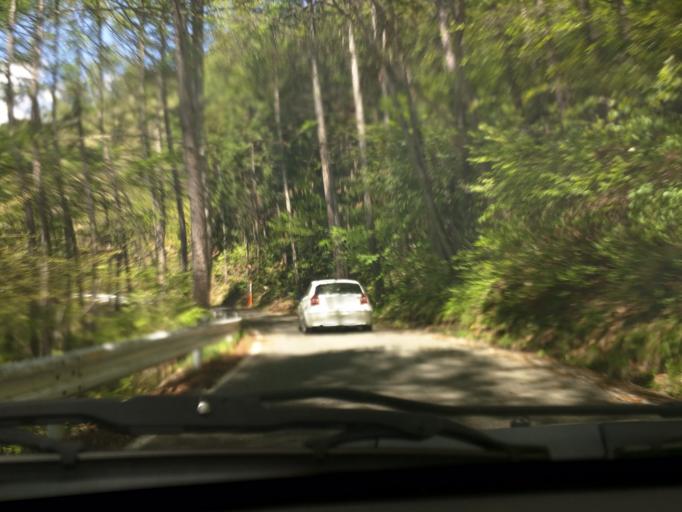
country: JP
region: Nagano
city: Nagano-shi
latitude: 36.6900
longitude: 138.1093
